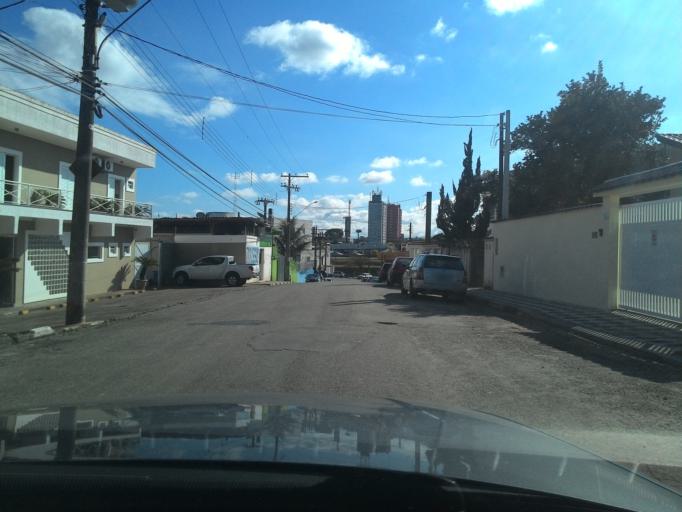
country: BR
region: Sao Paulo
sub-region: Registro
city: Registro
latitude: -24.4972
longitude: -47.8393
